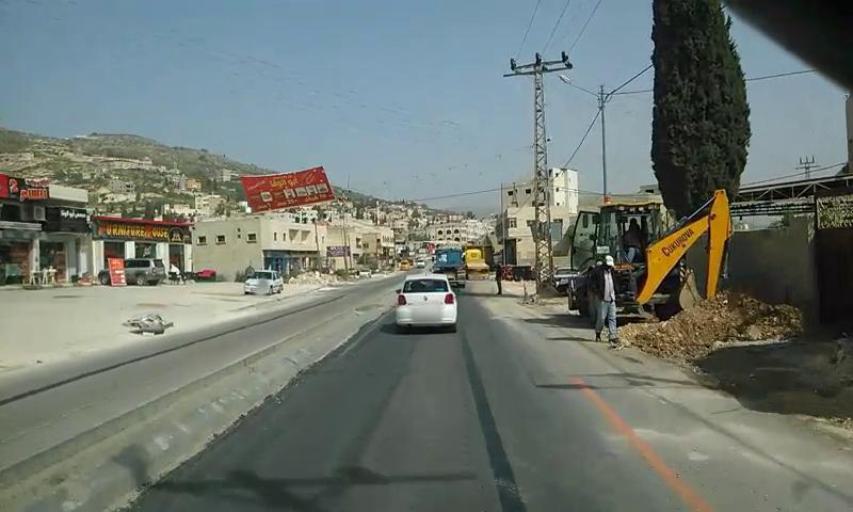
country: PS
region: West Bank
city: Huwwarah
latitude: 32.1463
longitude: 35.2579
